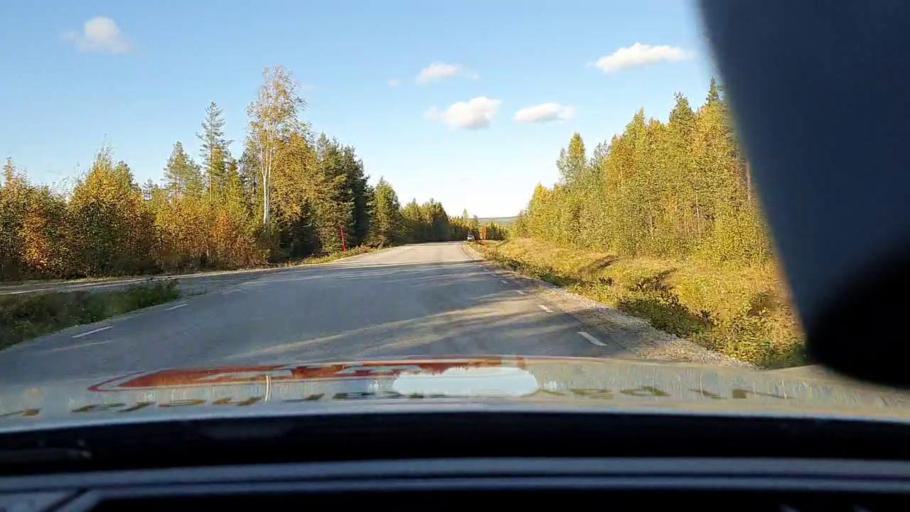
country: SE
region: Norrbotten
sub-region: Pitea Kommun
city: Norrfjarden
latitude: 65.5019
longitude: 21.4767
